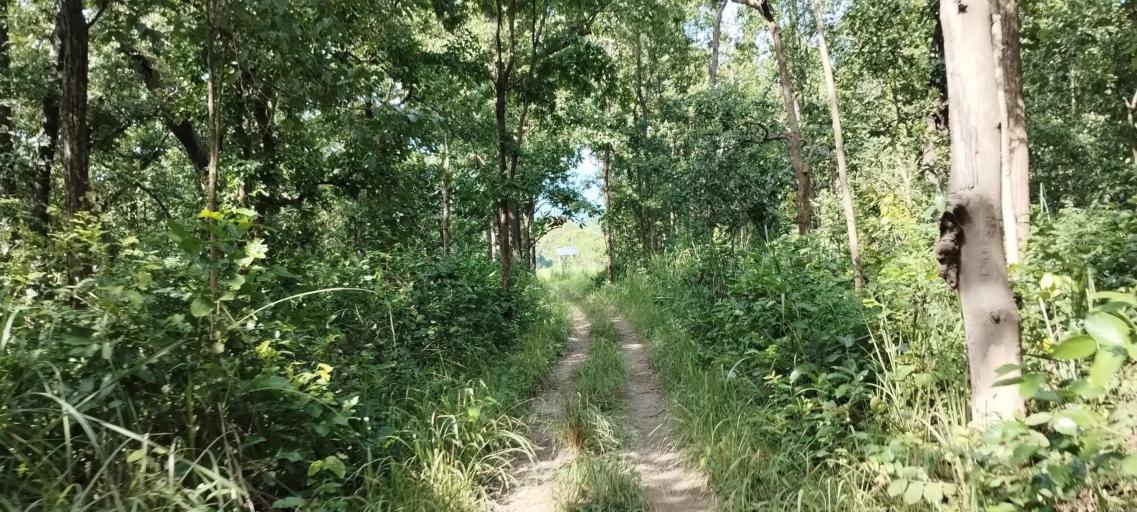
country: NP
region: Far Western
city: Tikapur
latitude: 28.5588
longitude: 81.2944
